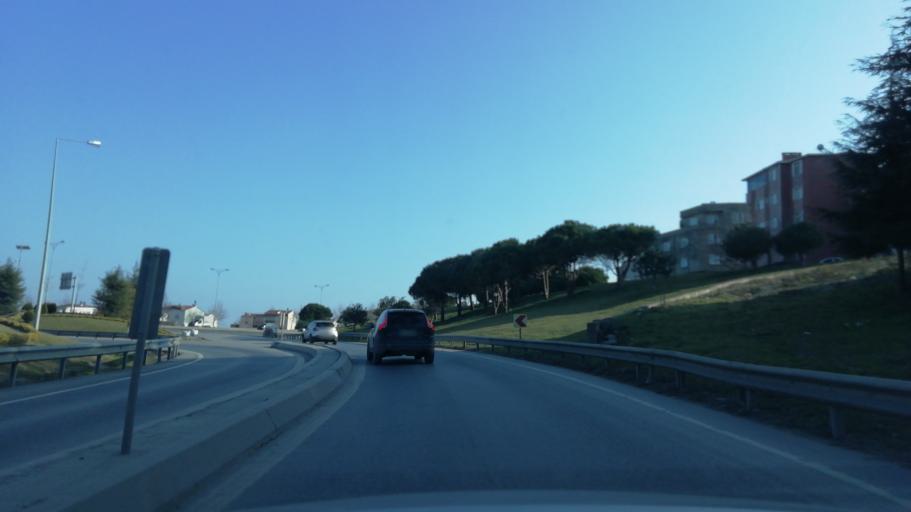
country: TR
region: Istanbul
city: Esenyurt
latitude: 41.0464
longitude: 28.6892
